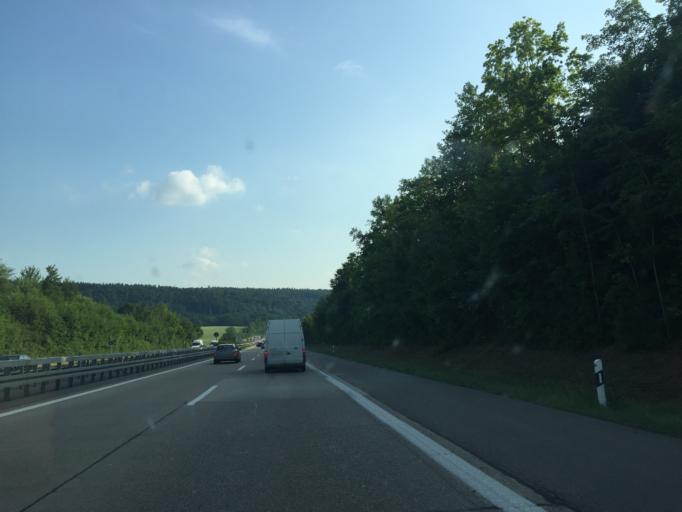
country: DE
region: Baden-Wuerttemberg
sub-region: Regierungsbezirk Stuttgart
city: Eberstadt
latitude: 49.1827
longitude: 9.3414
